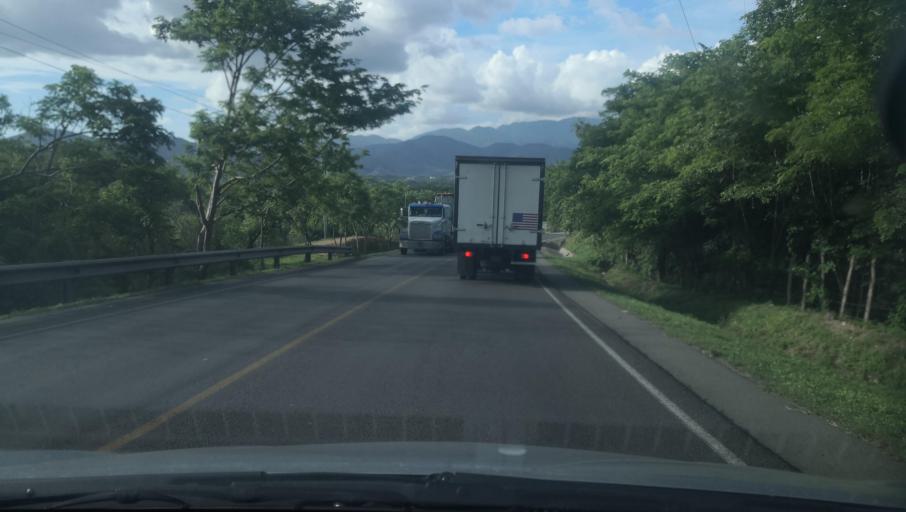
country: NI
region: Nueva Segovia
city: Ocotal
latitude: 13.6038
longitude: -86.4718
